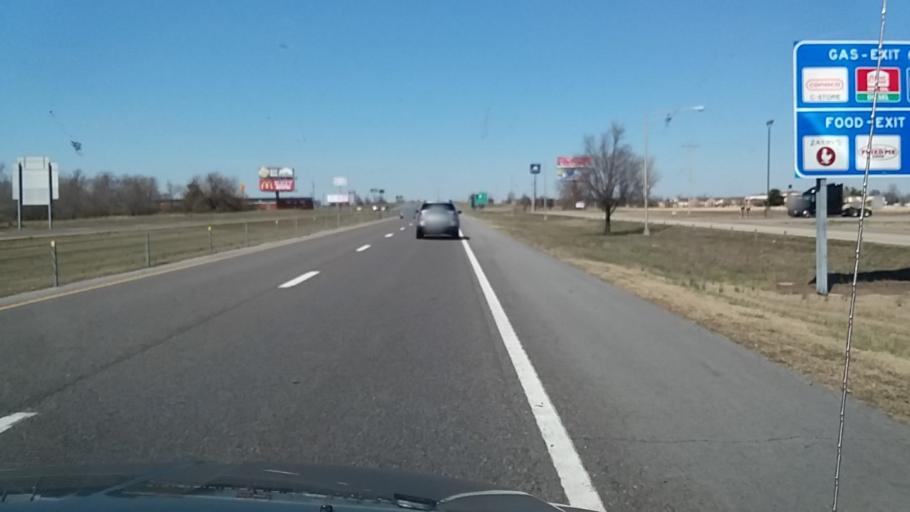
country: US
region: Missouri
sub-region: Scott County
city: Sikeston
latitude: 36.8848
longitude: -89.5331
